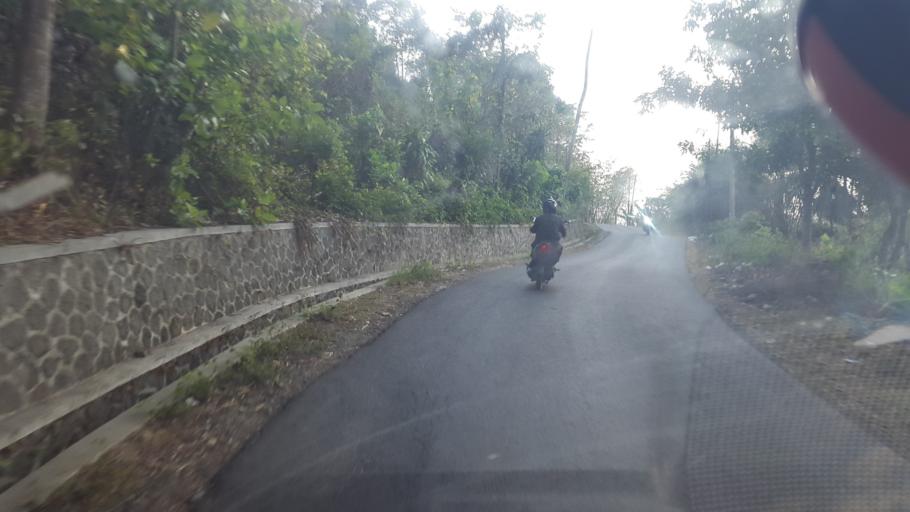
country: ID
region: West Java
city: Pondokaso
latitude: -7.3512
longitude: 106.5333
